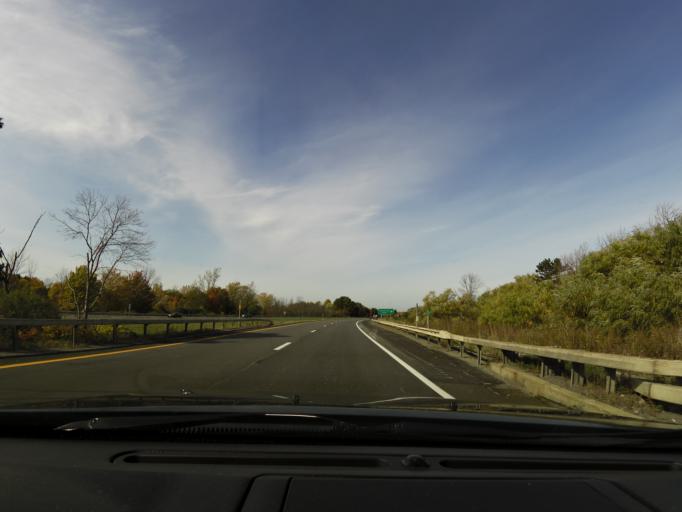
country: US
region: New York
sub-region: Erie County
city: Billington Heights
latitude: 42.7995
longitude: -78.6368
